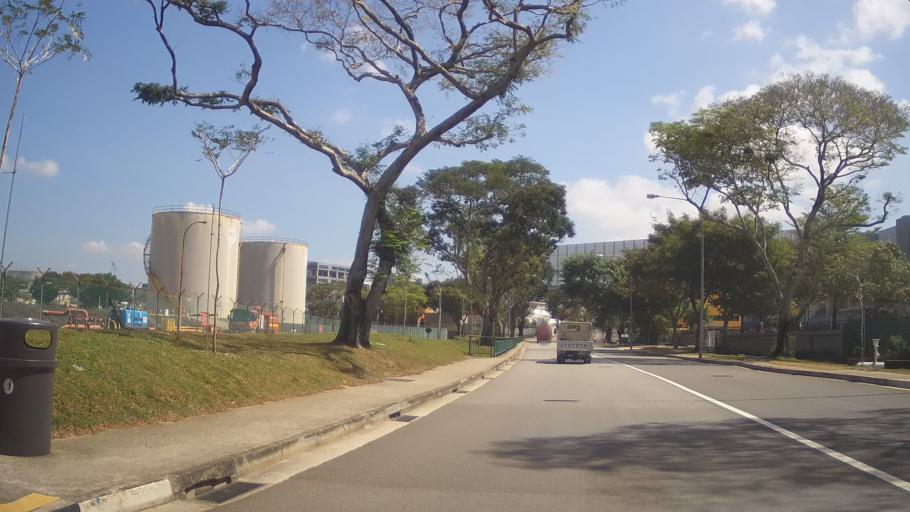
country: SG
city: Singapore
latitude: 1.3053
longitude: 103.6924
